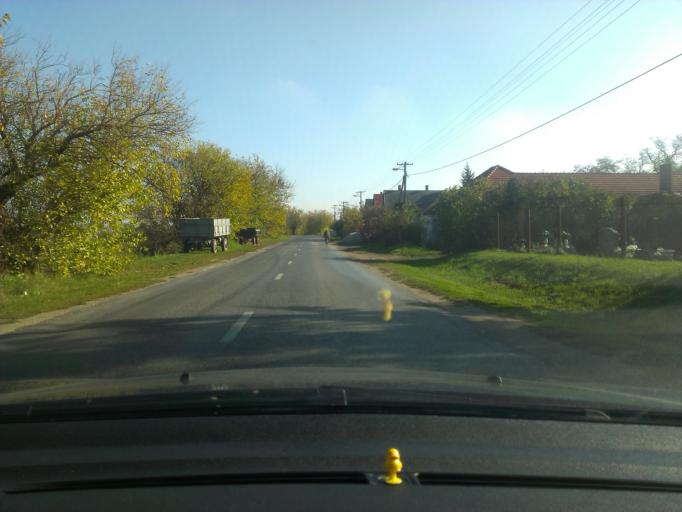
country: HU
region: Komarom-Esztergom
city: Komarom
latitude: 47.7239
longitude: 18.1653
